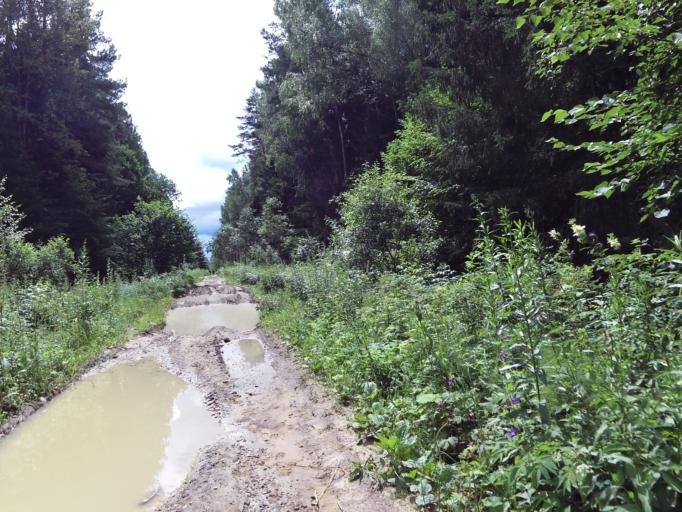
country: RU
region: Moskovskaya
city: Popovo
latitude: 54.9803
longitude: 37.6941
